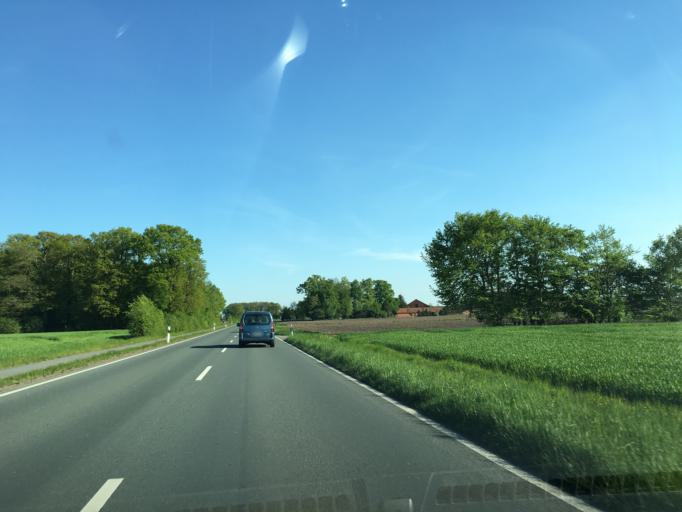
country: DE
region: North Rhine-Westphalia
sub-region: Regierungsbezirk Munster
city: Senden
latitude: 51.8419
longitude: 7.5143
